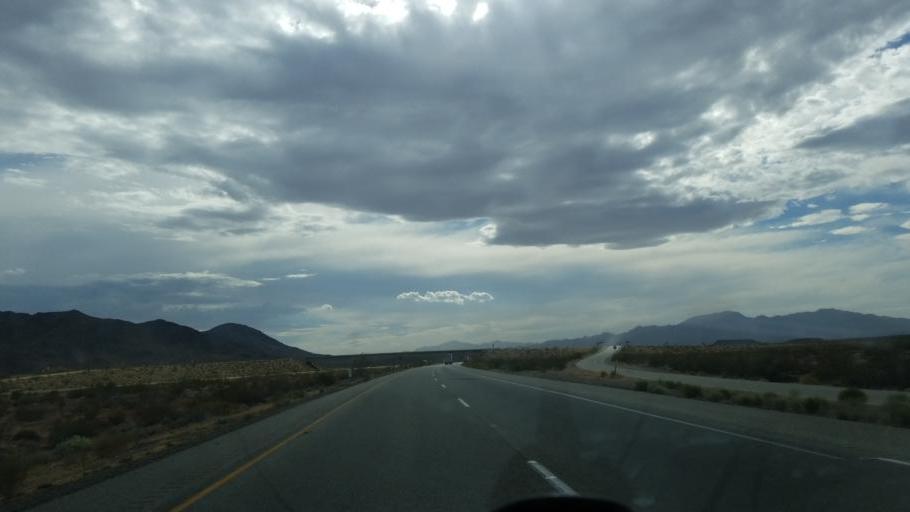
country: US
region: California
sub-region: San Bernardino County
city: Needles
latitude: 34.8015
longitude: -115.3159
